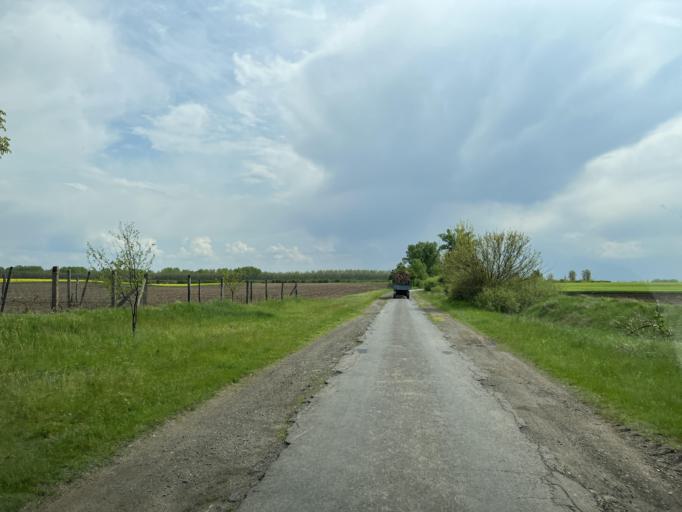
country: HU
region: Pest
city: Nagykoros
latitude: 47.0012
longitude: 19.7993
